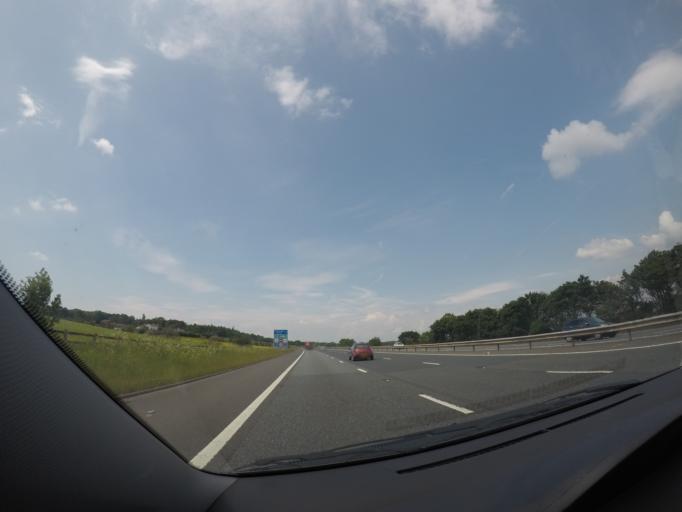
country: GB
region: England
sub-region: Cumbria
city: Scotby
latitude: 54.7866
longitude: -2.8613
